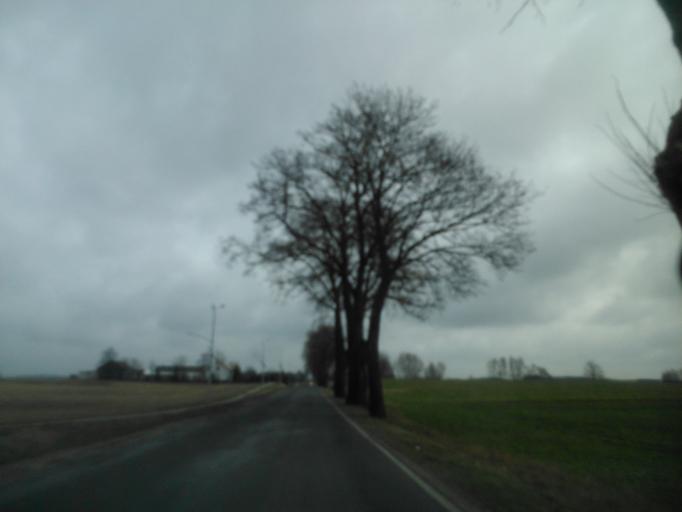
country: PL
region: Kujawsko-Pomorskie
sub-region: Powiat golubsko-dobrzynski
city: Kowalewo Pomorskie
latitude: 53.1588
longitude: 18.9280
